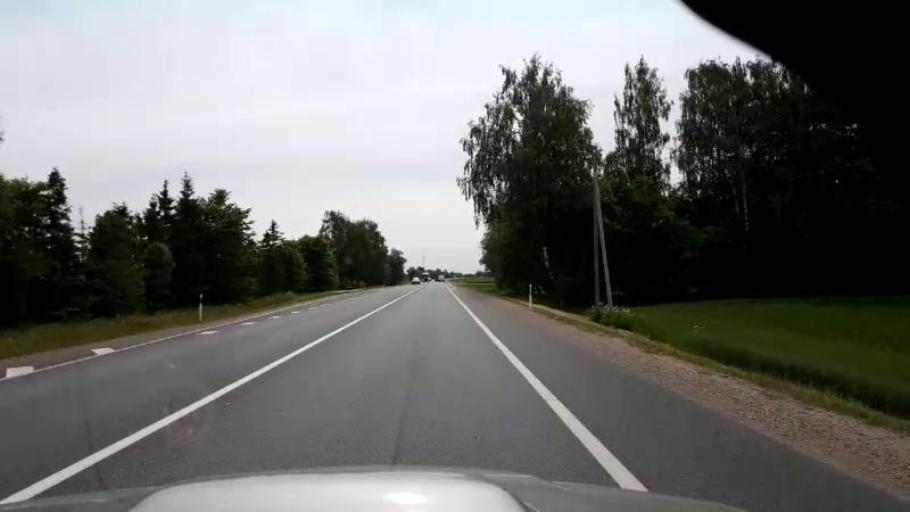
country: LV
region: Bauskas Rajons
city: Bauska
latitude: 56.4378
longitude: 24.1737
